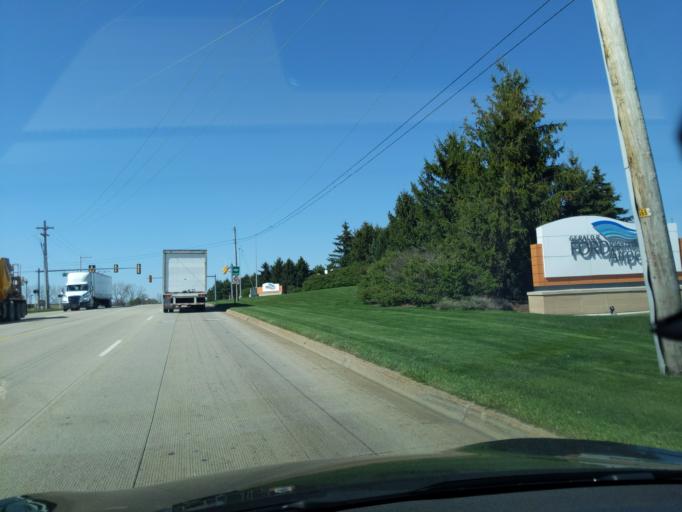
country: US
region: Michigan
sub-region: Kent County
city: East Grand Rapids
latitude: 42.8826
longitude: -85.5470
